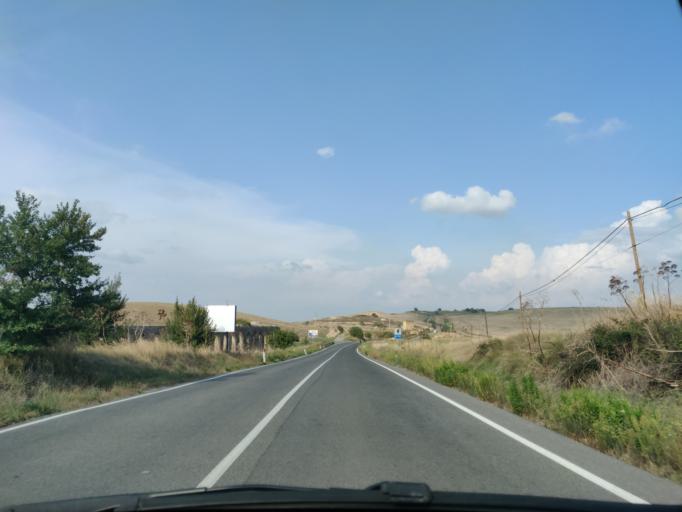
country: IT
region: Latium
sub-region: Provincia di Viterbo
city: Tarquinia
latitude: 42.2510
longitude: 11.8115
